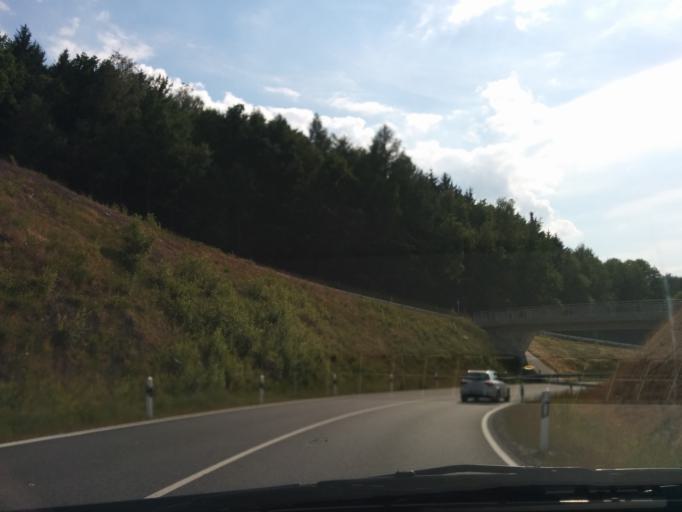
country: DE
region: Saxony
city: Niederwiesa
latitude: 50.8631
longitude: 13.0386
